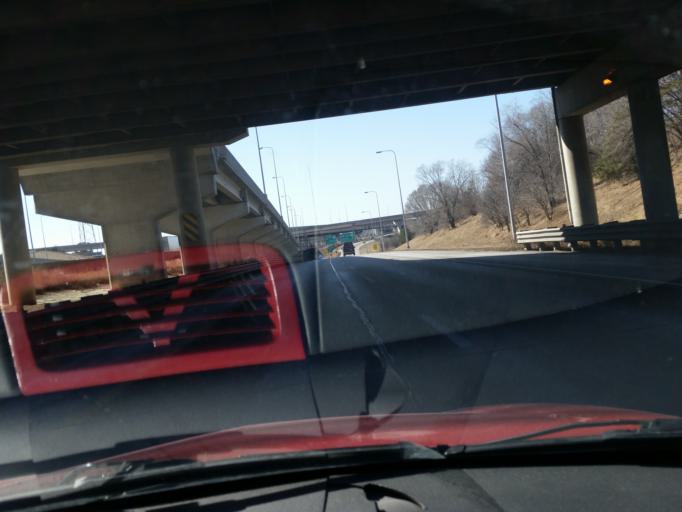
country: US
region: Nebraska
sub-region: Douglas County
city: Omaha
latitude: 41.2265
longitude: -95.9469
